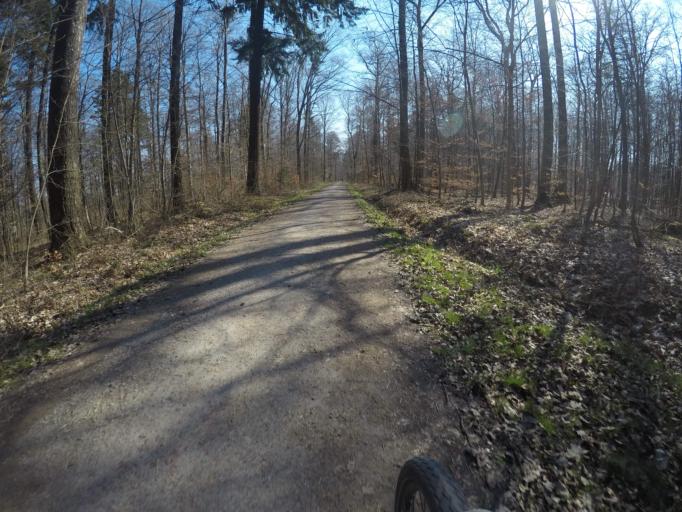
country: DE
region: Baden-Wuerttemberg
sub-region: Regierungsbezirk Stuttgart
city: Gerlingen
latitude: 48.7521
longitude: 9.1070
